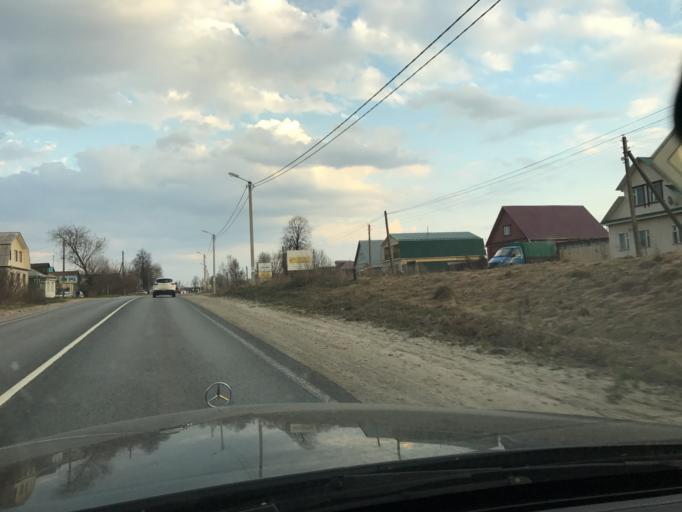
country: RU
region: Vladimir
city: Murom
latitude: 55.6127
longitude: 41.9486
